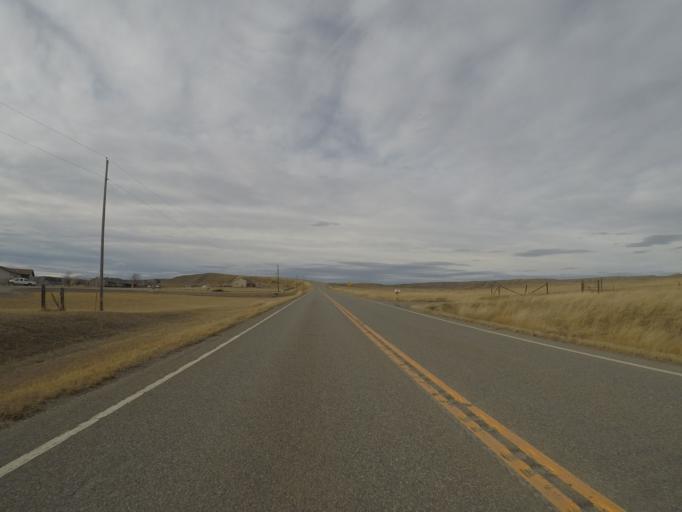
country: US
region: Montana
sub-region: Yellowstone County
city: Laurel
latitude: 45.8429
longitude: -108.7248
